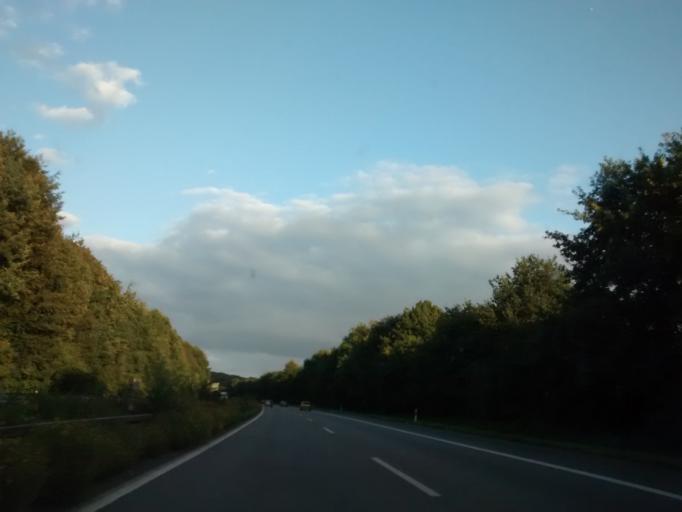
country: DE
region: North Rhine-Westphalia
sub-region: Regierungsbezirk Munster
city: Tecklenburg
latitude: 52.2527
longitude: 7.7893
